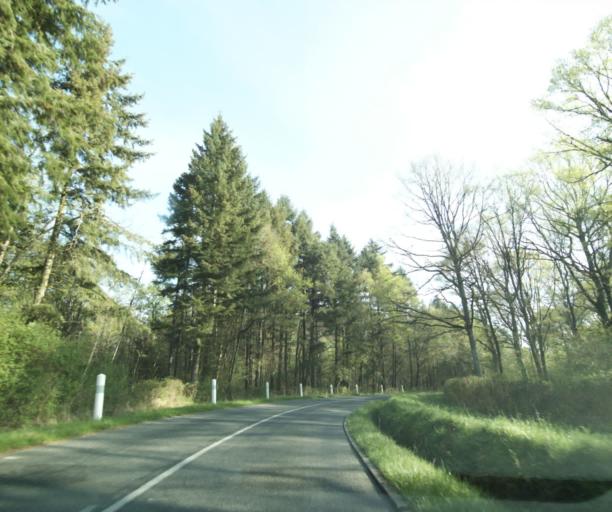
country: FR
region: Ile-de-France
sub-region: Departement de Seine-et-Marne
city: Vernou-la-Celle-sur-Seine
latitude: 48.4356
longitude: 2.8499
